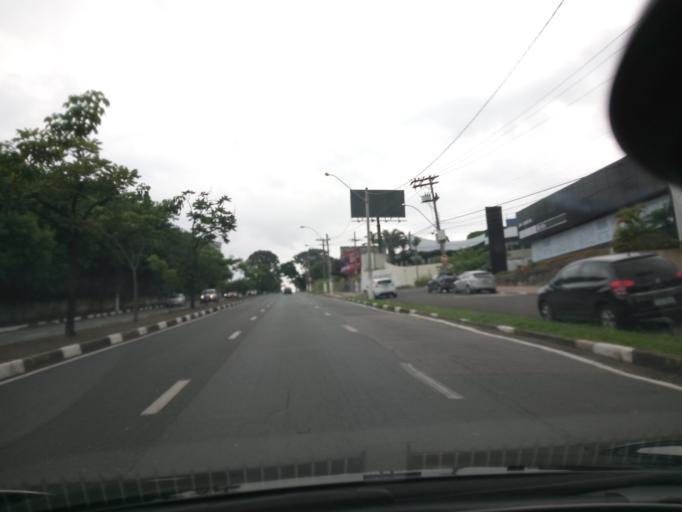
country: BR
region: Sao Paulo
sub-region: Campinas
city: Campinas
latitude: -22.9047
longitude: -47.0354
